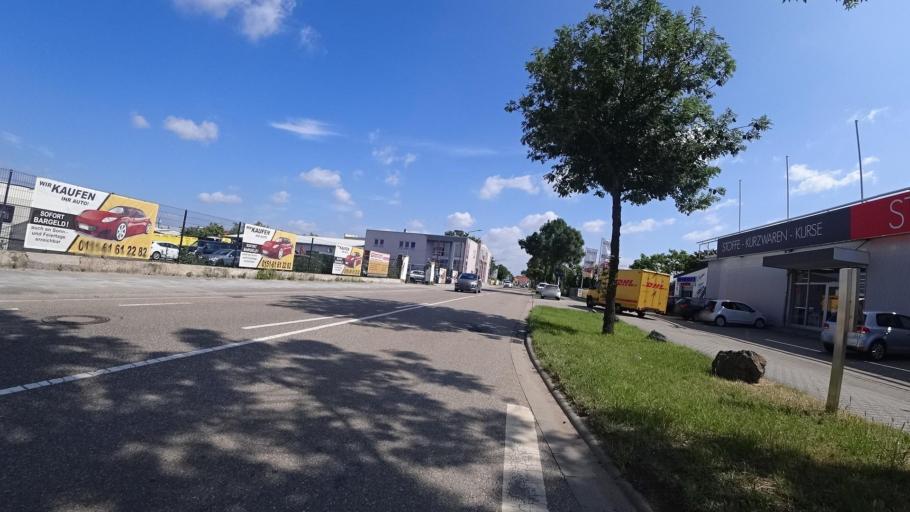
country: DE
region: Rheinland-Pfalz
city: Worms
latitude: 49.6201
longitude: 8.3589
